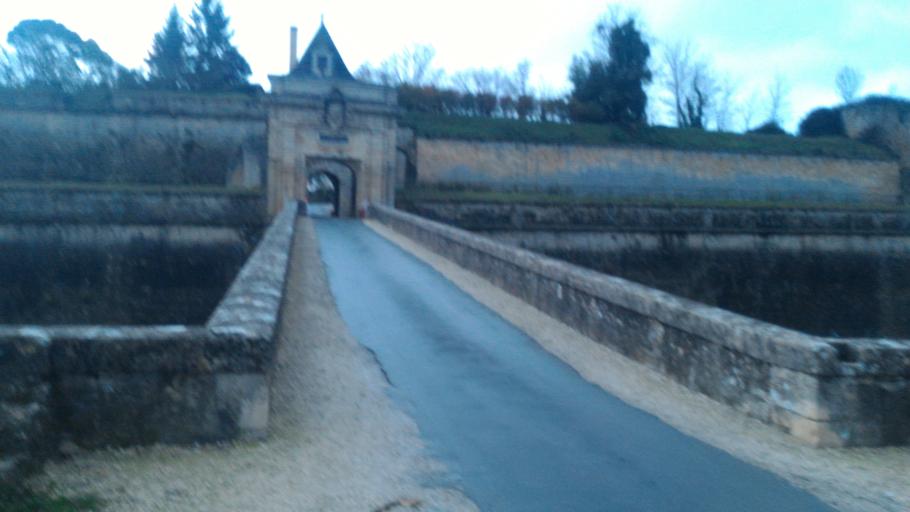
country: FR
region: Aquitaine
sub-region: Departement de la Gironde
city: Blaye
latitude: 45.1298
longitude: -0.6645
